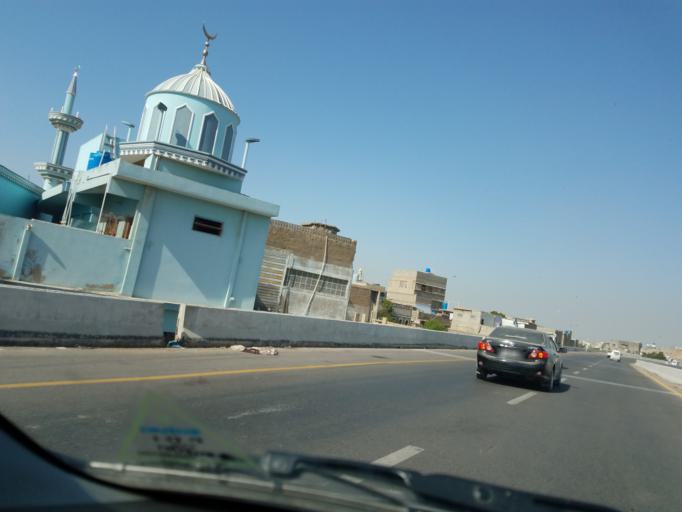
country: PK
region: Sindh
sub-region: Karachi District
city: Karachi
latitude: 24.8816
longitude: 67.0177
